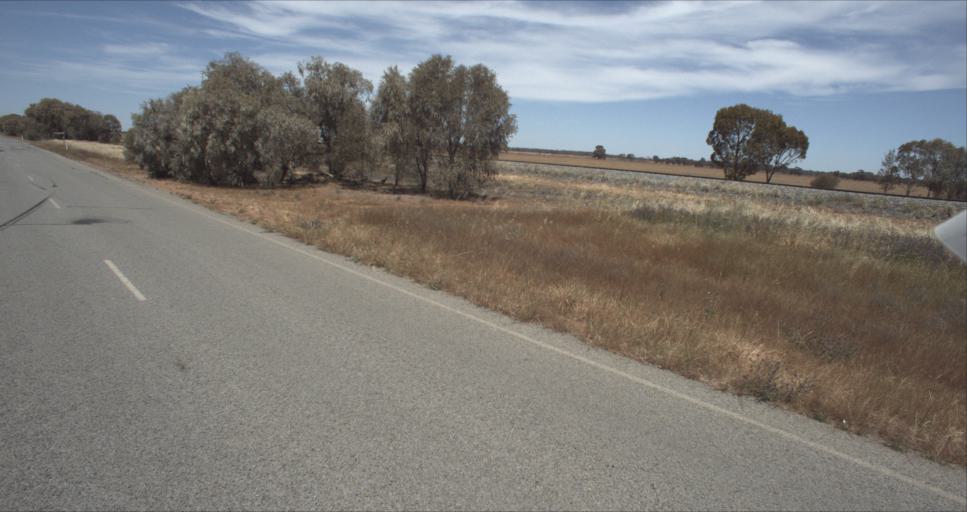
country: AU
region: New South Wales
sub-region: Leeton
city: Leeton
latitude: -34.6289
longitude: 146.4544
